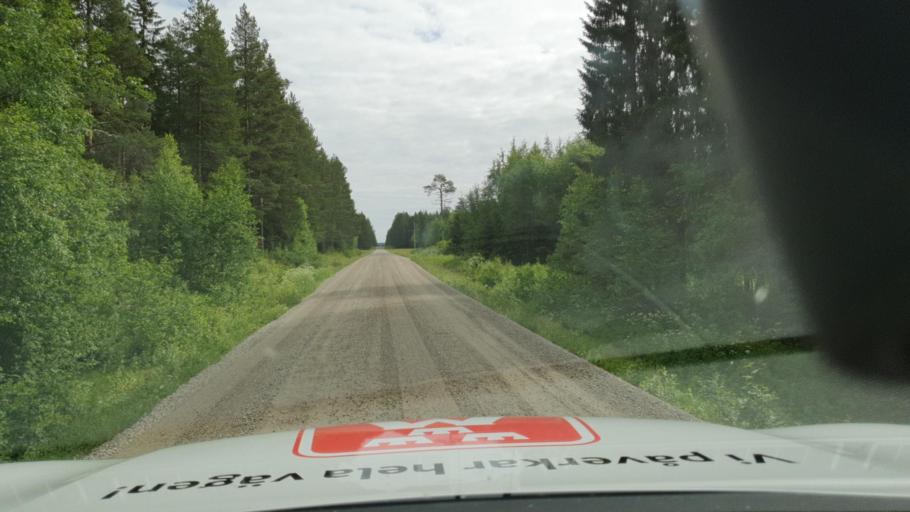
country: SE
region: Vaesterbotten
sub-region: Skelleftea Kommun
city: Forsbacka
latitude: 64.6560
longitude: 20.4121
